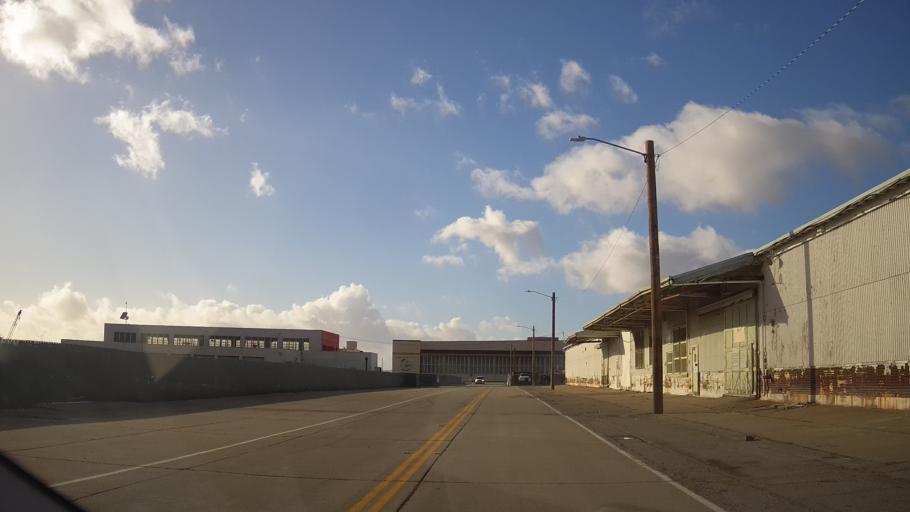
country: US
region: California
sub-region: Alameda County
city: Oakland
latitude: 37.7819
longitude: -122.2952
